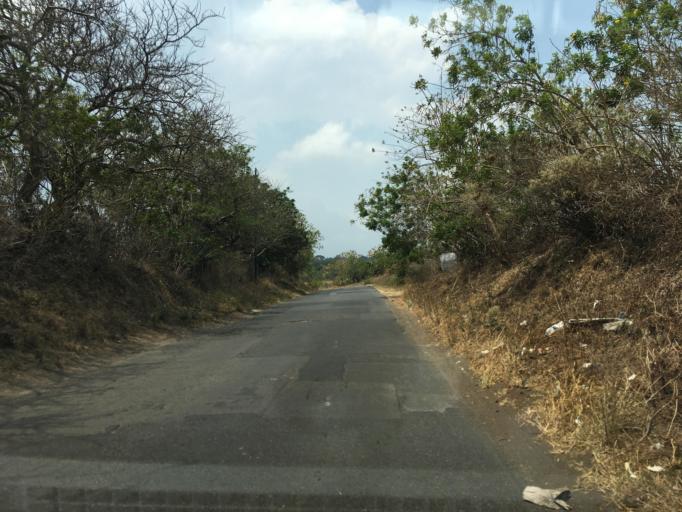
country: GT
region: Escuintla
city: San Vicente Pacaya
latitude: 14.3600
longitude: -90.5700
